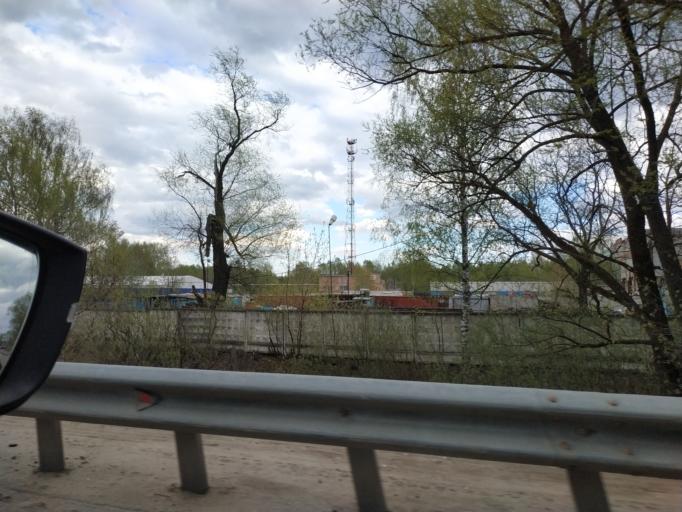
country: RU
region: Moskovskaya
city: Pavlovskiy Posad
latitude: 55.7946
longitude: 38.6524
